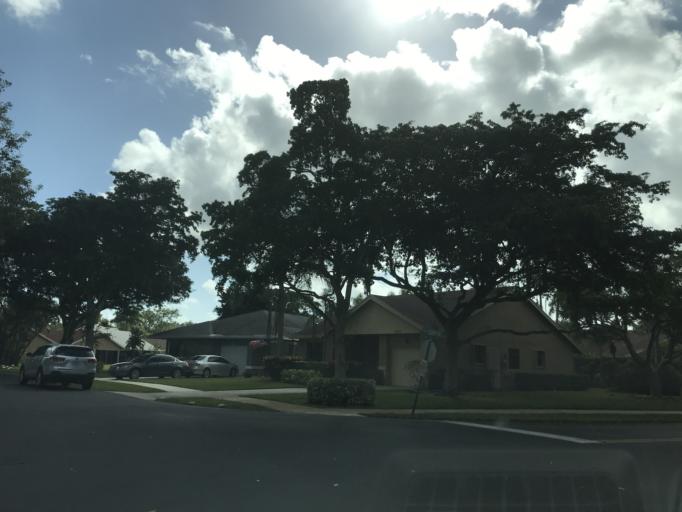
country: US
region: Florida
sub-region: Broward County
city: Coconut Creek
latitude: 26.2611
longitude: -80.1894
